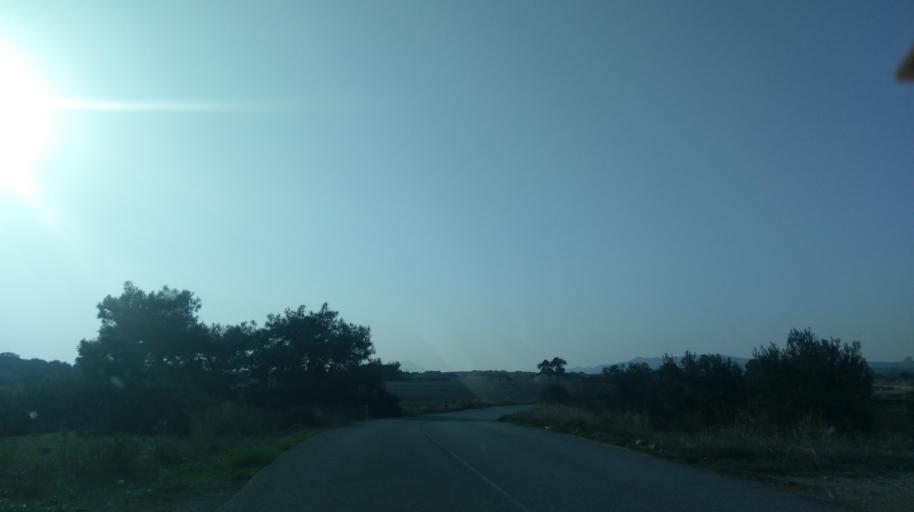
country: CY
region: Ammochostos
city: Leonarisso
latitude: 35.4308
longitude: 34.0547
